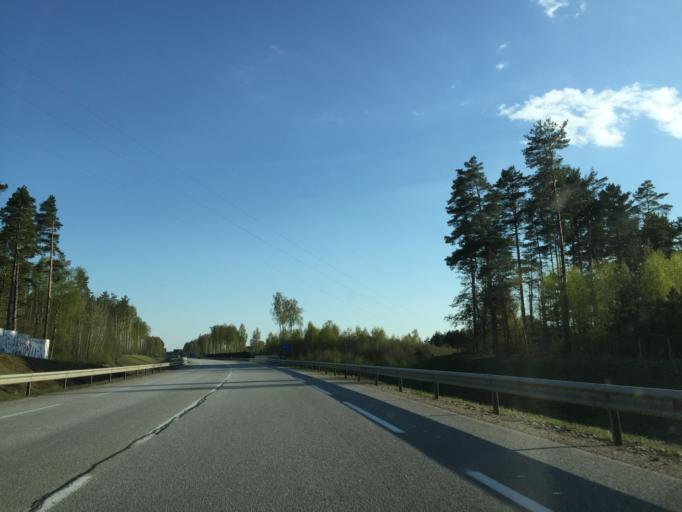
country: LV
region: Saulkrastu
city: Saulkrasti
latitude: 57.2617
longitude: 24.4310
